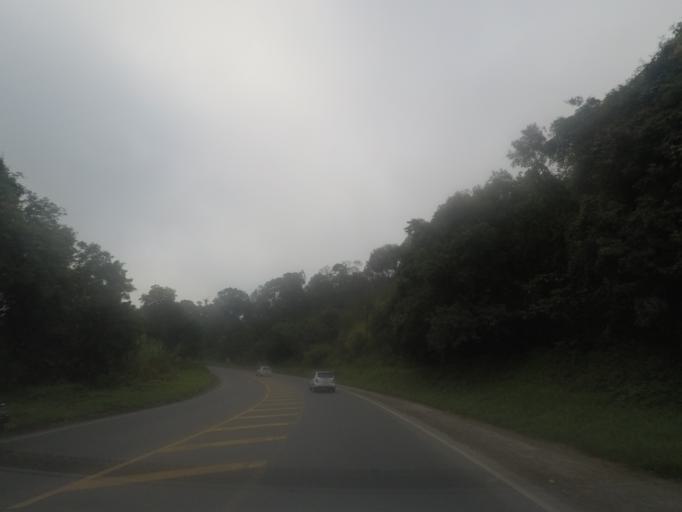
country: BR
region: Parana
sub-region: Almirante Tamandare
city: Almirante Tamandare
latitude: -25.2880
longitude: -49.3079
